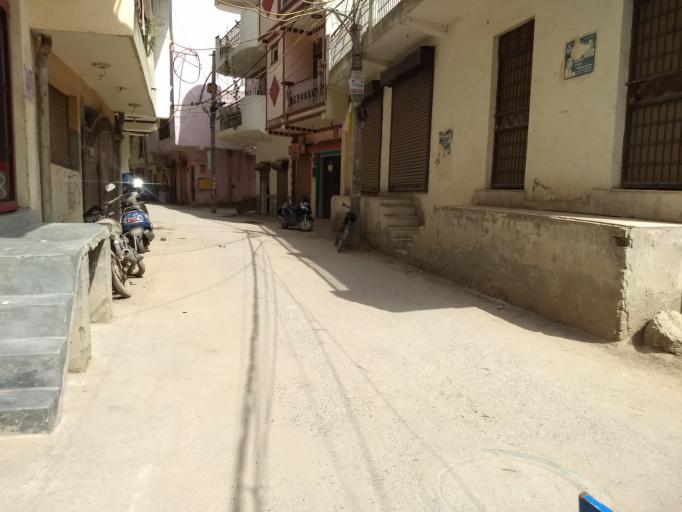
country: IN
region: Haryana
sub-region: Gurgaon
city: Gurgaon
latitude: 28.5407
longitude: 77.1253
